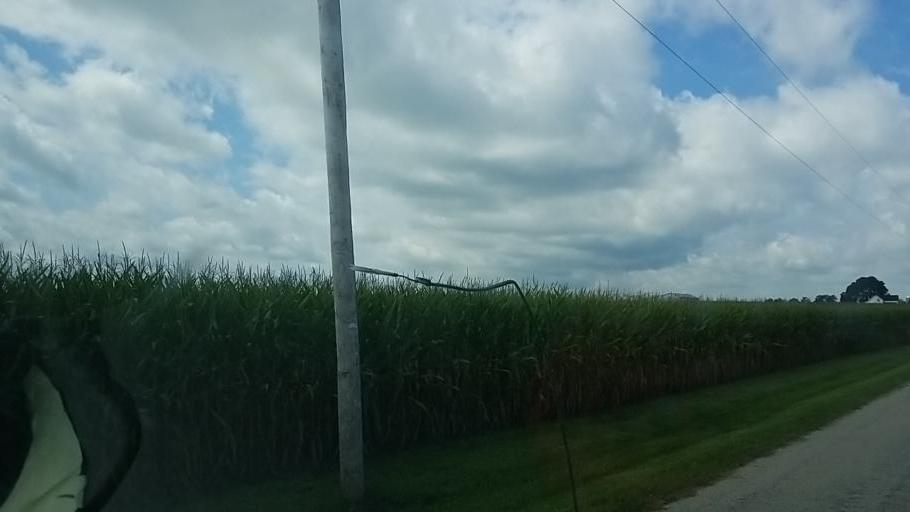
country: US
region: Ohio
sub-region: Madison County
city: Bethel
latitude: 39.7171
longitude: -83.4368
